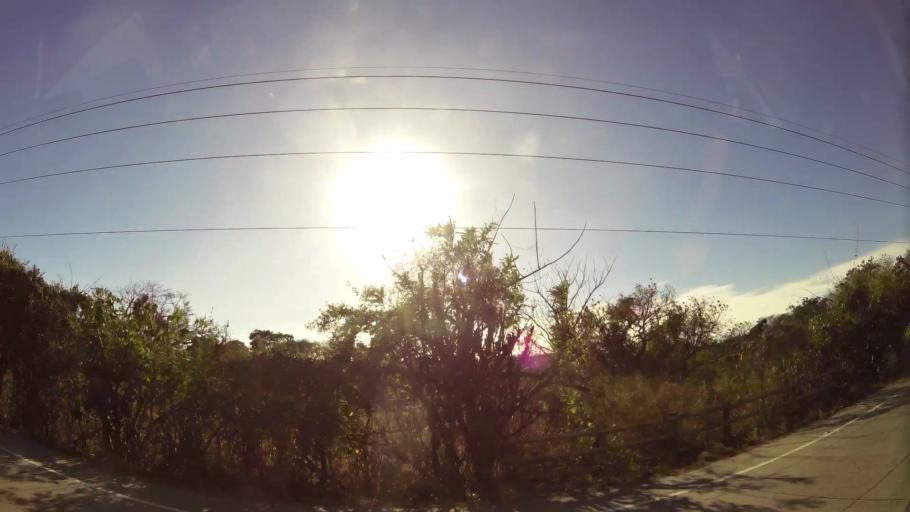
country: SV
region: Santa Ana
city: Metapan
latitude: 14.2355
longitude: -89.4683
